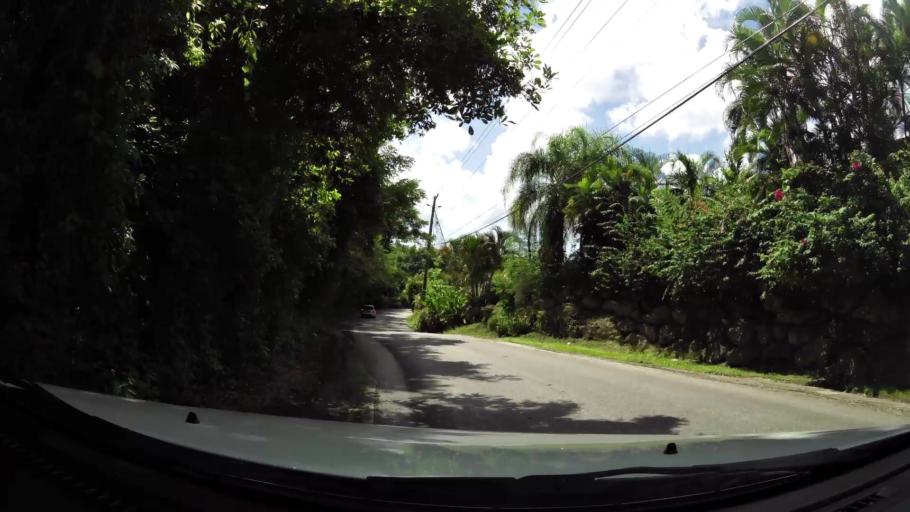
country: BB
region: Saint James
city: Holetown
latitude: 13.2003
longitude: -59.6350
